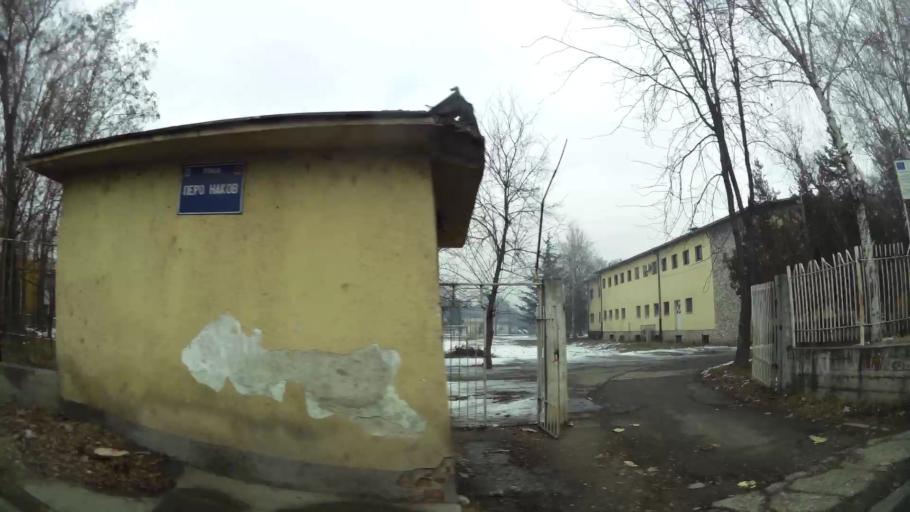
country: MK
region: Cair
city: Cair
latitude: 41.9968
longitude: 21.4768
